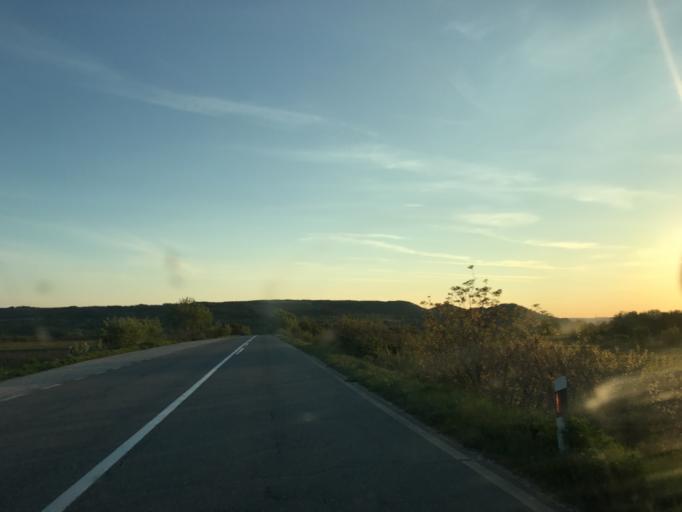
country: RO
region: Mehedinti
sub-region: Comuna Gogosu
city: Ostrovu Mare
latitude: 44.4057
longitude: 22.4780
